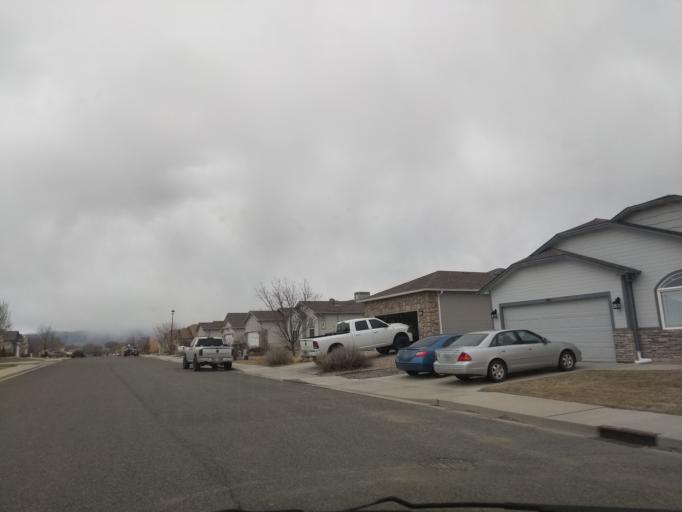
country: US
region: Colorado
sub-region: Mesa County
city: Fruitvale
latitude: 39.0882
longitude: -108.5244
